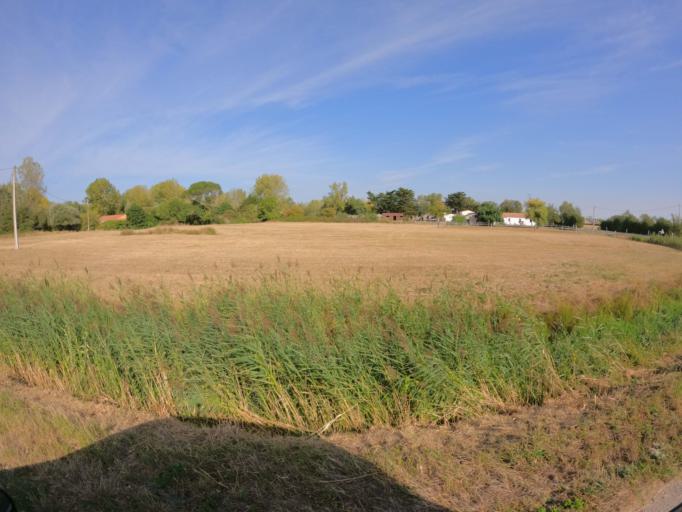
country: FR
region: Pays de la Loire
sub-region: Departement de la Vendee
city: Le Perrier
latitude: 46.8118
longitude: -1.9883
